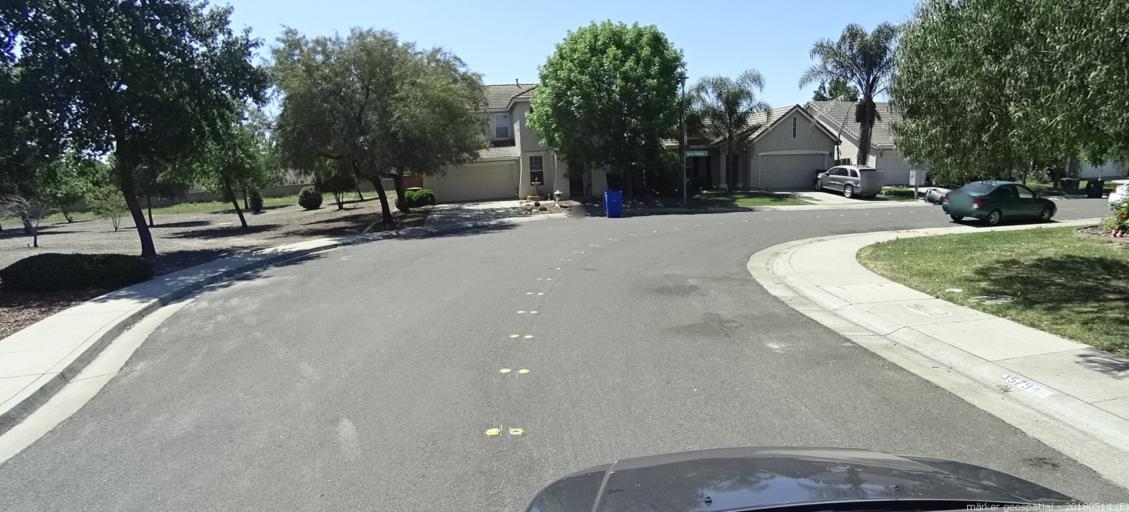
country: US
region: California
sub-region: Yolo County
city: West Sacramento
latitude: 38.6342
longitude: -121.5269
